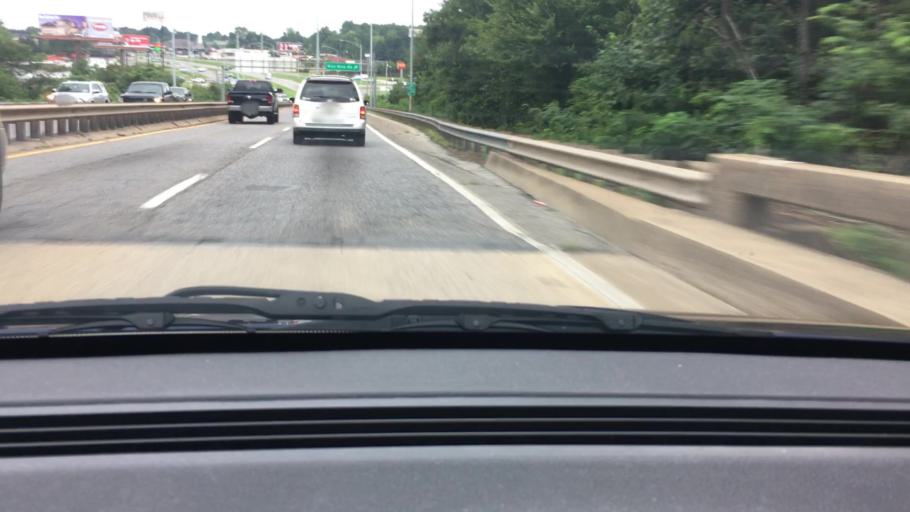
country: US
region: Alabama
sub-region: Tuscaloosa County
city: Tuscaloosa
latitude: 33.2250
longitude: -87.5324
